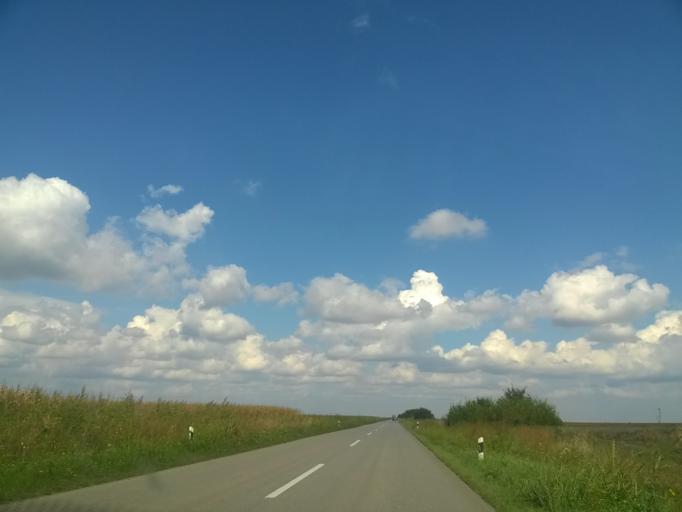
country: RS
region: Autonomna Pokrajina Vojvodina
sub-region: Juznobanatski Okrug
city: Alibunar
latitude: 45.0991
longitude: 20.9902
